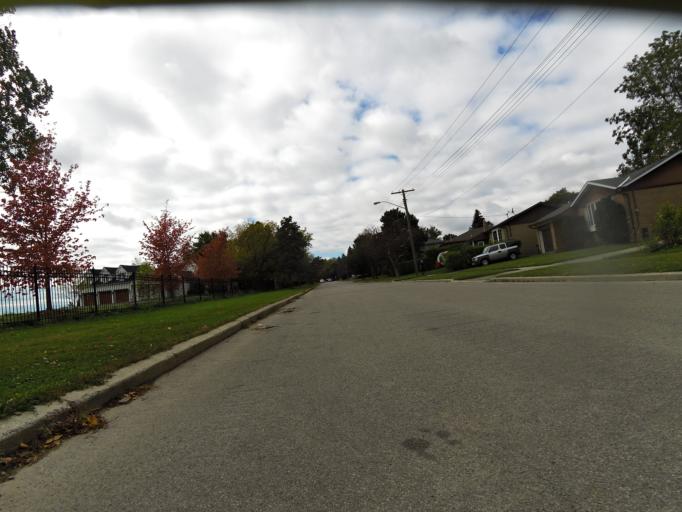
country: CA
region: Ontario
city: Scarborough
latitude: 43.7540
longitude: -79.1777
